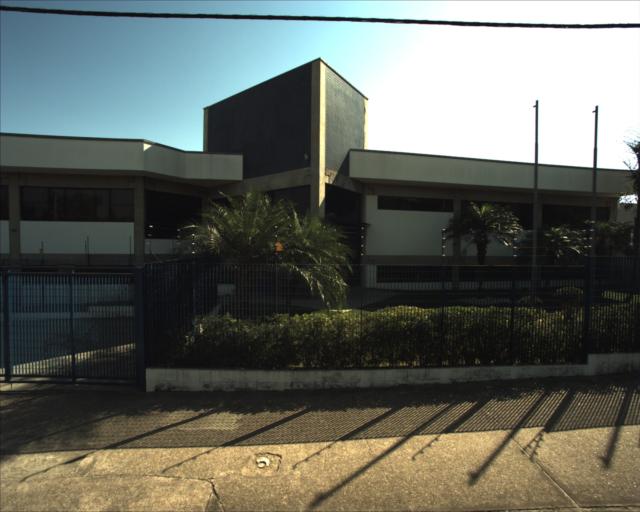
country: BR
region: Sao Paulo
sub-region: Sorocaba
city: Sorocaba
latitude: -23.4917
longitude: -47.4333
